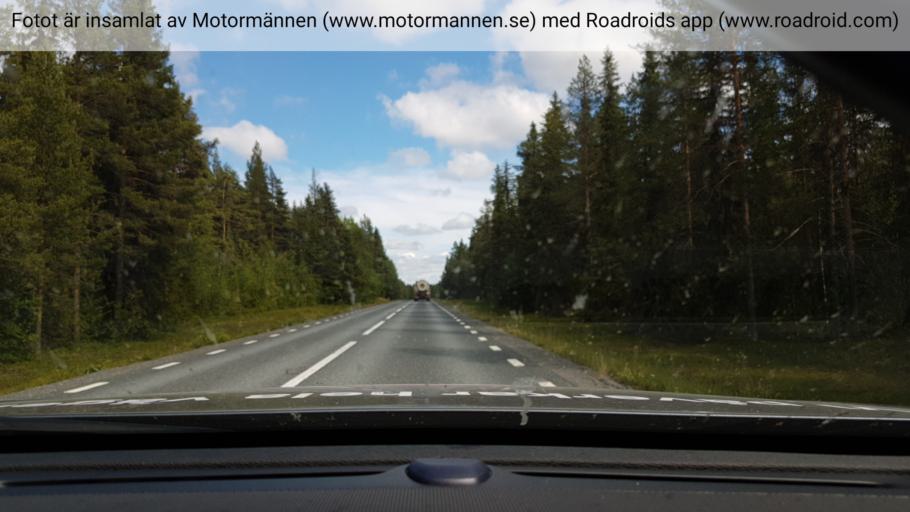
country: SE
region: Vaesterbotten
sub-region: Sorsele Kommun
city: Sorsele
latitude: 65.5590
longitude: 17.8258
